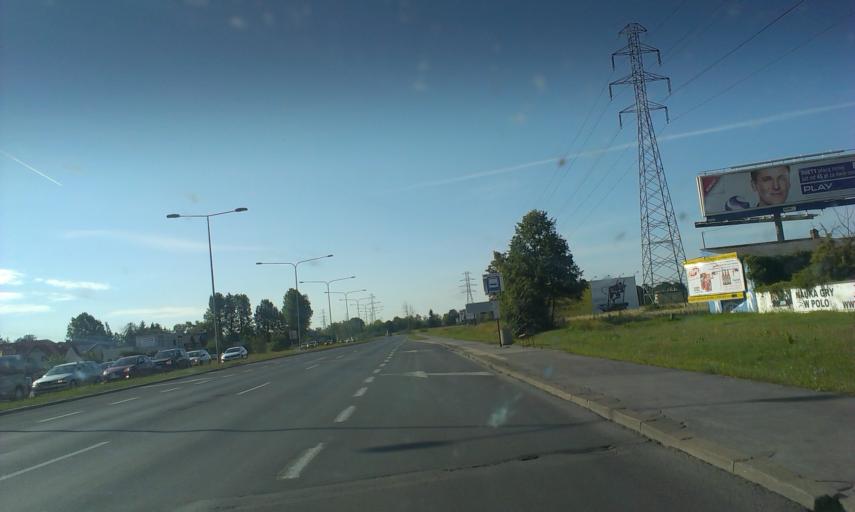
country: PL
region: Masovian Voivodeship
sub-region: Warszawa
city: Kabaty
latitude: 52.1224
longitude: 21.0975
